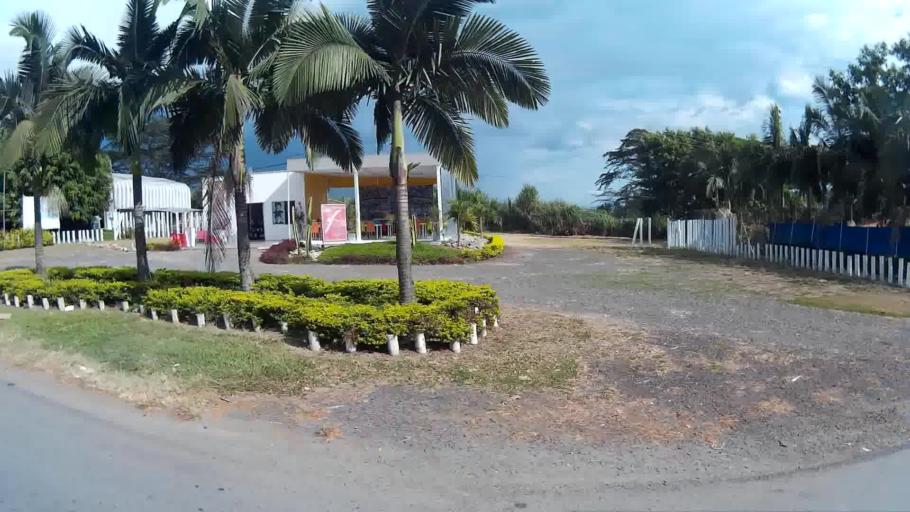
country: CO
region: Valle del Cauca
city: Cartago
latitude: 4.8064
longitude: -75.8178
